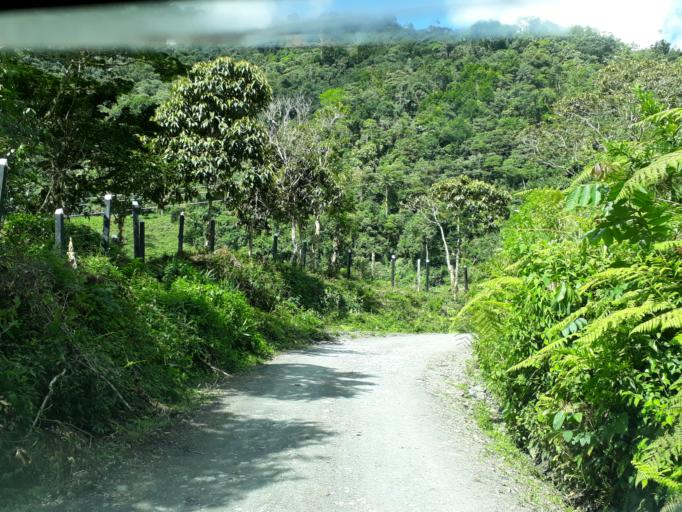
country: CO
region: Cundinamarca
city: Topaipi
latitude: 5.3966
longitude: -74.1994
